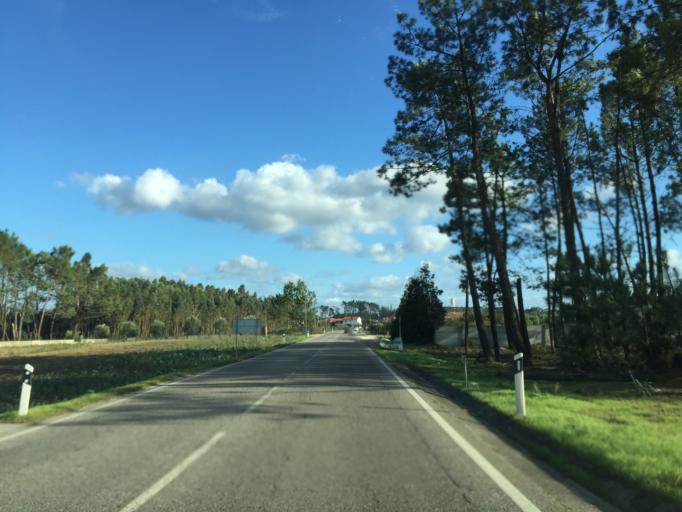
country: PT
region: Leiria
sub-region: Pombal
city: Lourical
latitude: 39.9735
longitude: -8.7961
